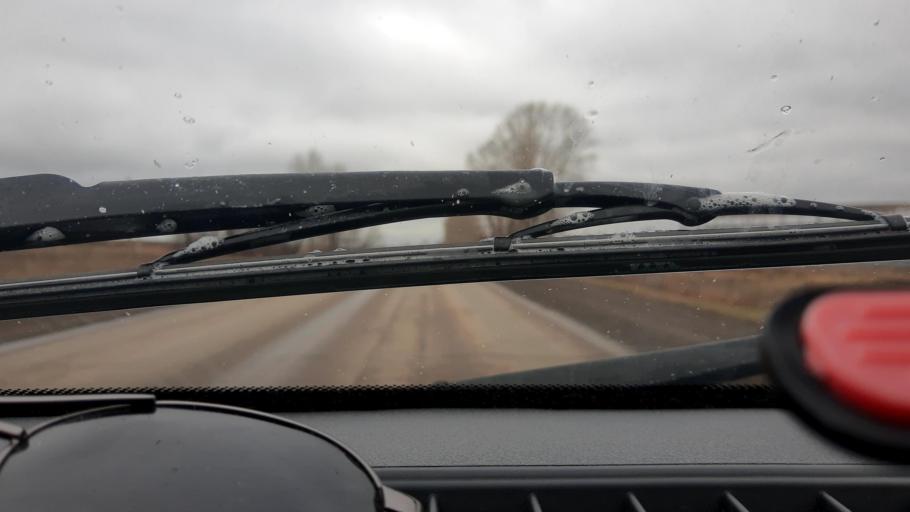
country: RU
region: Bashkortostan
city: Avdon
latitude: 54.7241
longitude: 55.8075
